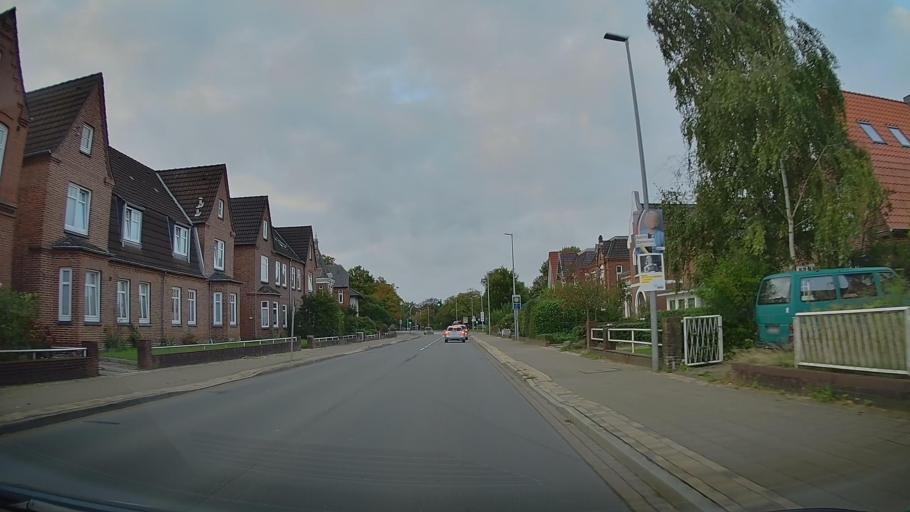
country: DE
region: Schleswig-Holstein
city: Husum
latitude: 54.4818
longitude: 9.0554
